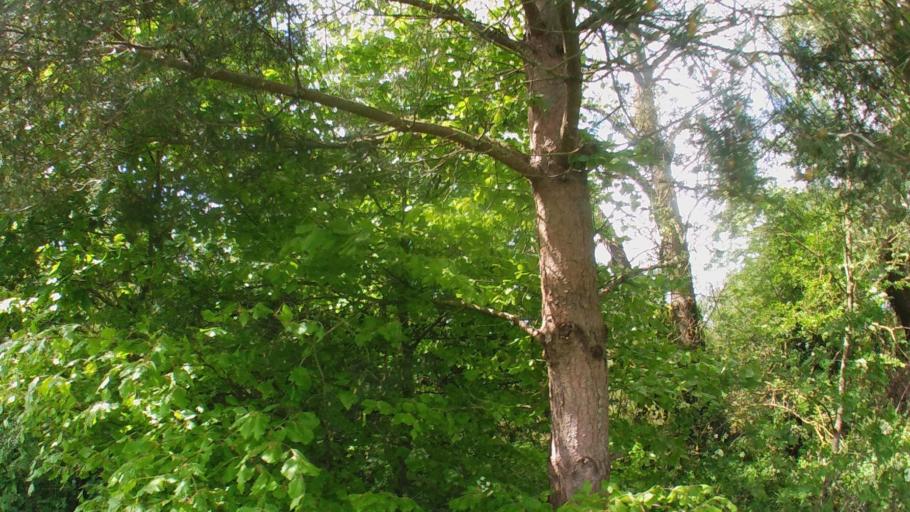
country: IE
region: Leinster
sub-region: Kilkenny
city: Thomastown
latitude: 52.5938
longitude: -7.1852
